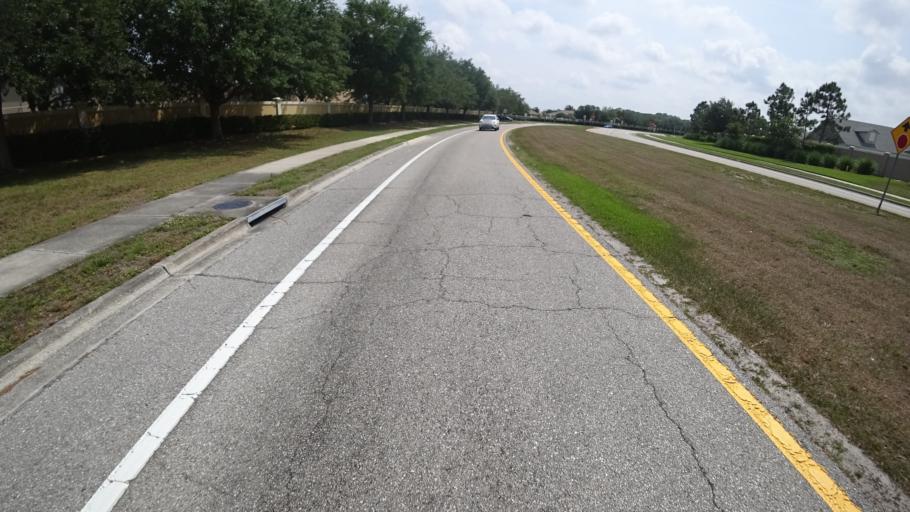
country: US
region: Florida
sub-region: Sarasota County
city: North Sarasota
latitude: 27.4196
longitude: -82.5143
